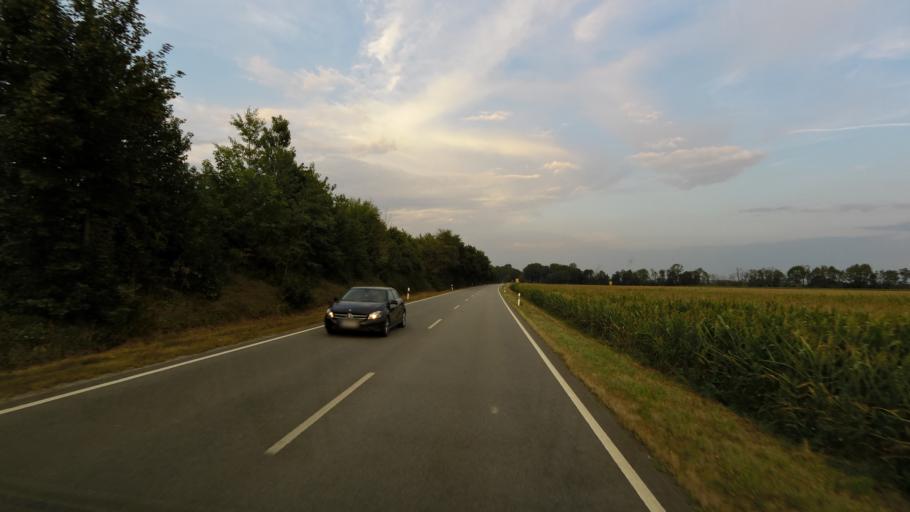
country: DE
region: Bavaria
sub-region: Lower Bavaria
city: Kirchham
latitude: 48.3501
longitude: 13.2835
